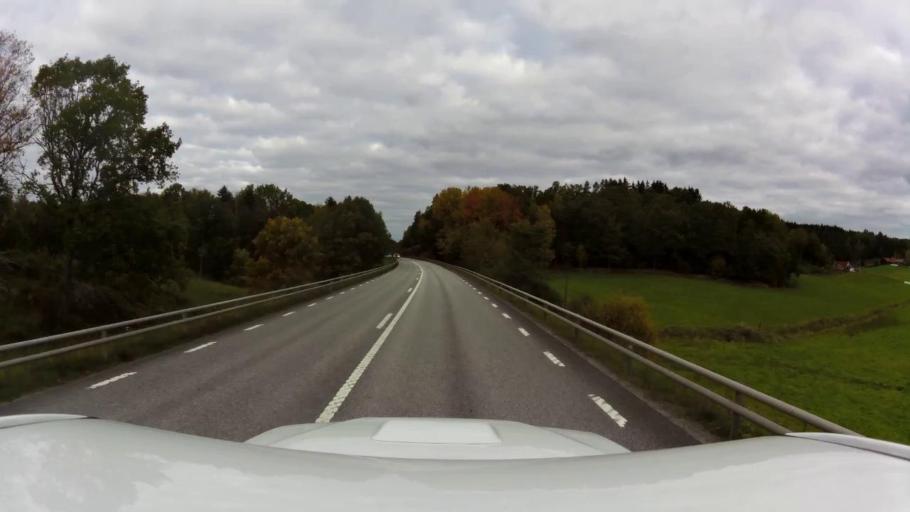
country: SE
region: OEstergoetland
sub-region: Kinda Kommun
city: Rimforsa
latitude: 58.1832
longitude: 15.6717
